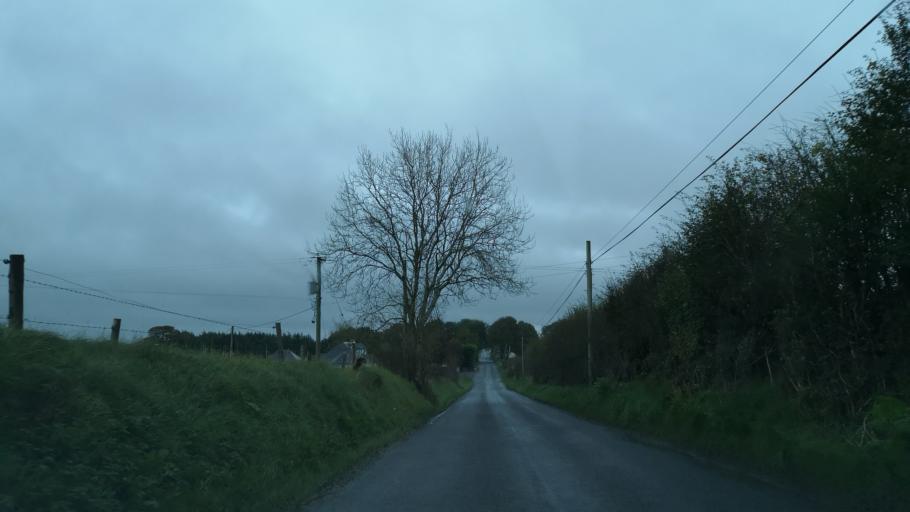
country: IE
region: Connaught
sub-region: Maigh Eo
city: Ballyhaunis
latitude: 53.7864
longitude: -8.7231
